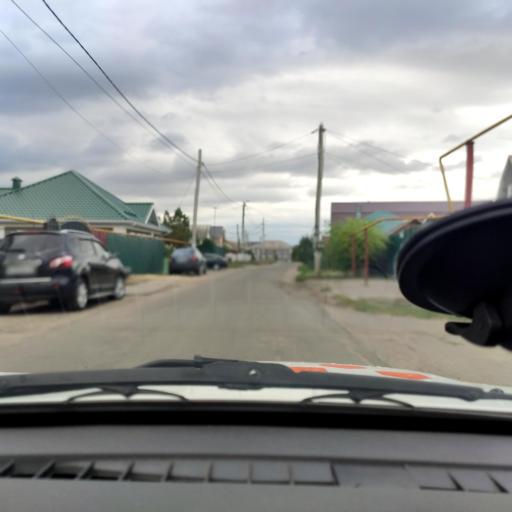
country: RU
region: Voronezj
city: Novaya Usman'
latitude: 51.6215
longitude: 39.4008
